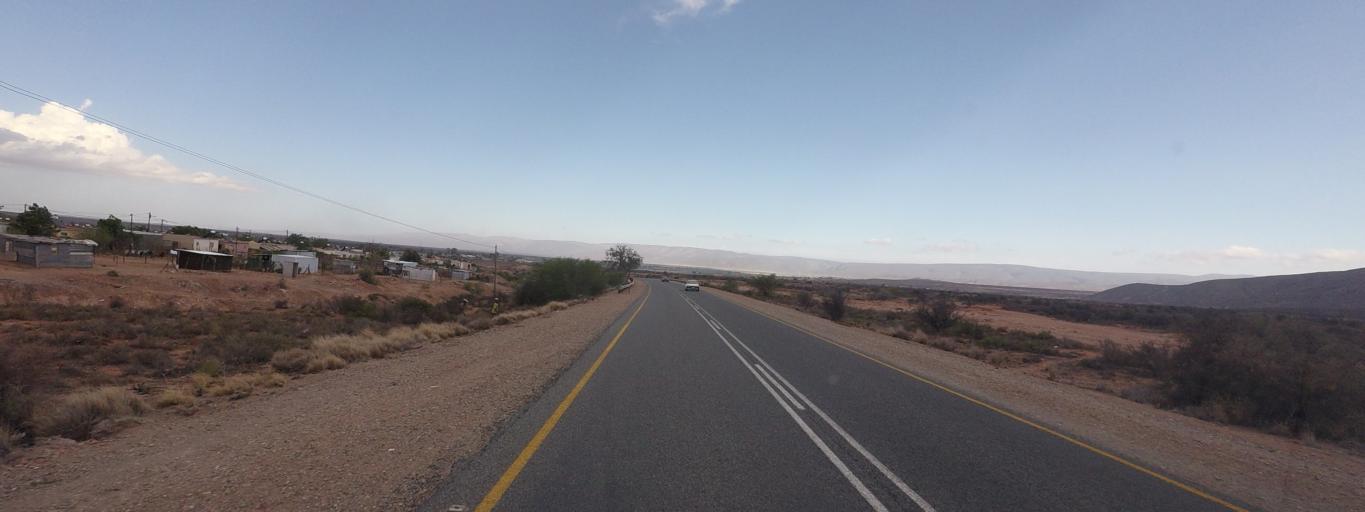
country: ZA
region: Western Cape
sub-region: Eden District Municipality
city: Ladismith
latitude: -33.5214
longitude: 21.6677
